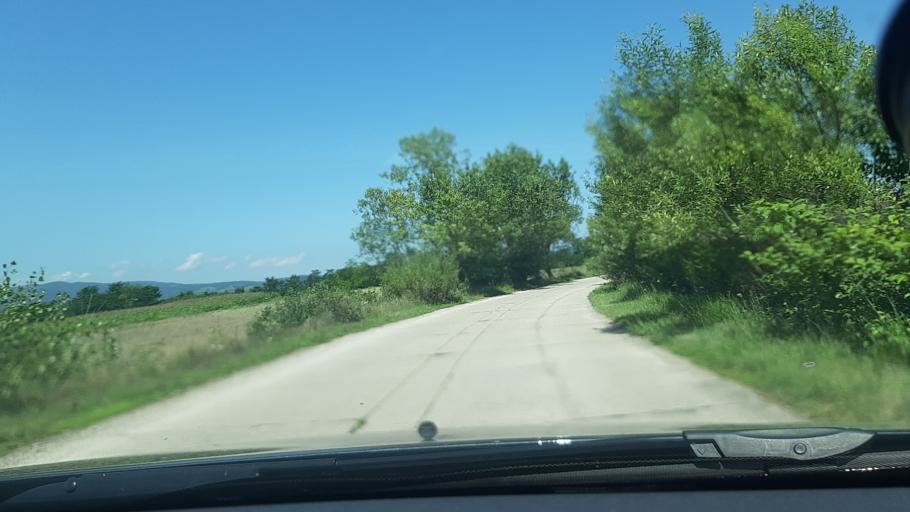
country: RO
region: Hunedoara
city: Bucium-Orlea
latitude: 45.5866
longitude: 22.9602
